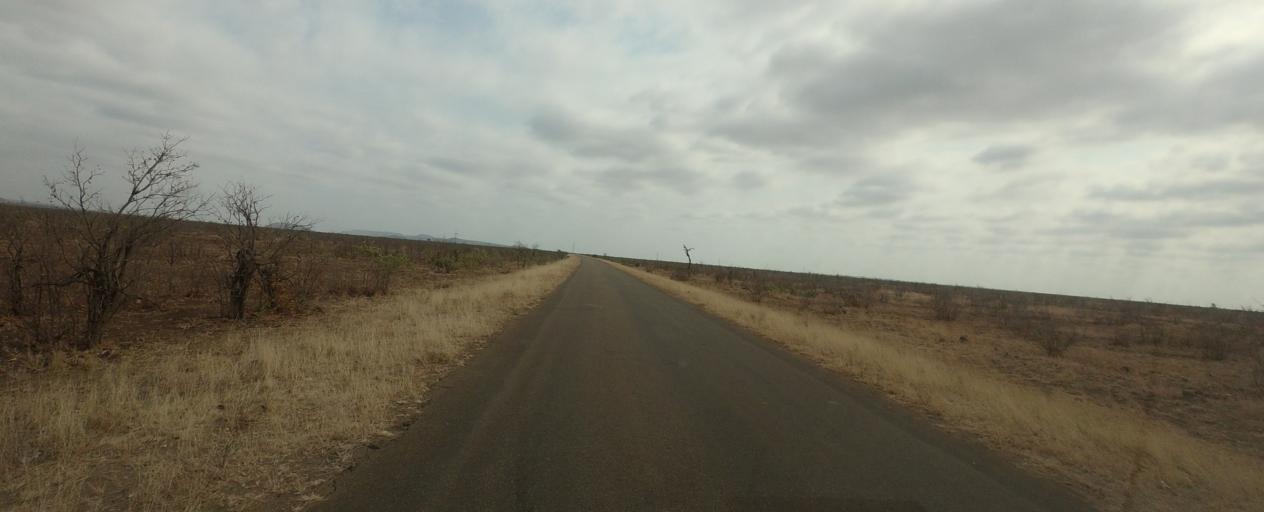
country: ZA
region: Limpopo
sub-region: Vhembe District Municipality
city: Mutale
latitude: -22.6742
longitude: 31.1676
